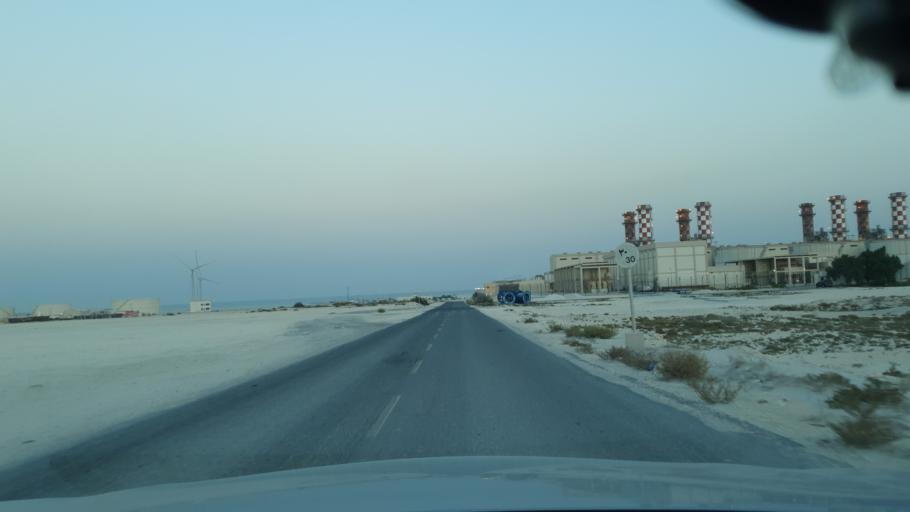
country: BH
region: Central Governorate
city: Dar Kulayb
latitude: 25.9740
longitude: 50.6037
